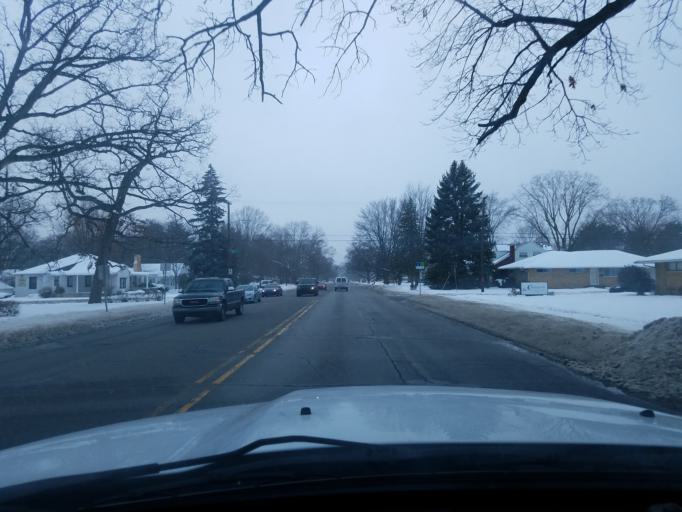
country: US
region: Indiana
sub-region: Saint Joseph County
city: Mishawaka
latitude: 41.6729
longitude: -86.1985
